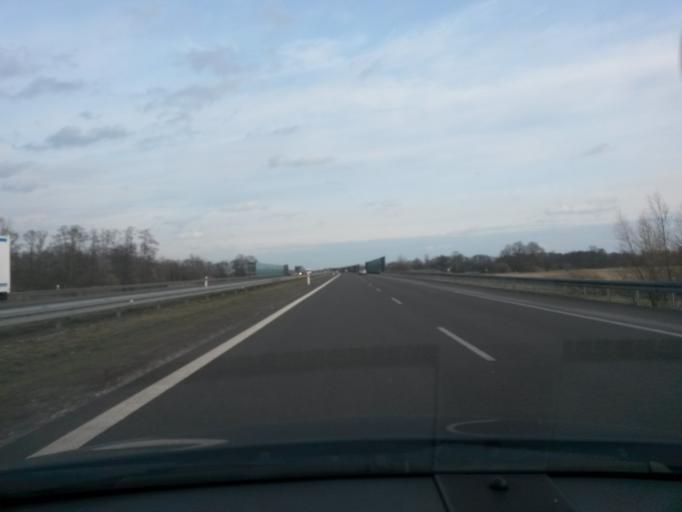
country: PL
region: Greater Poland Voivodeship
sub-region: Powiat turecki
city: Brudzew
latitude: 52.1255
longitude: 18.6751
